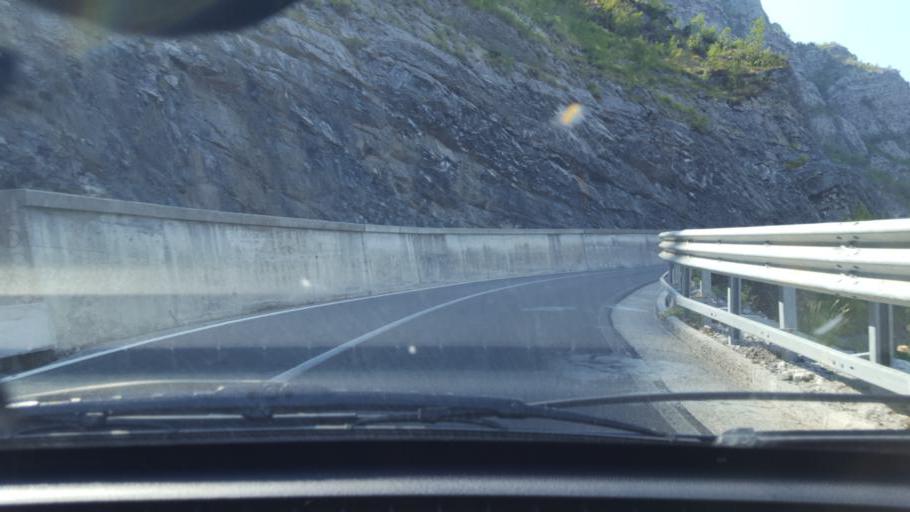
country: AL
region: Shkoder
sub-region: Rrethi i Malesia e Madhe
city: Kastrat
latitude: 42.4137
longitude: 19.4991
